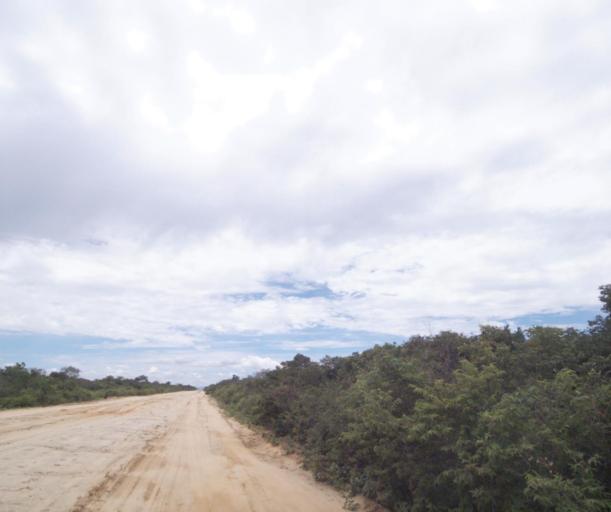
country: BR
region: Bahia
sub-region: Carinhanha
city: Carinhanha
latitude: -14.2605
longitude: -43.8224
